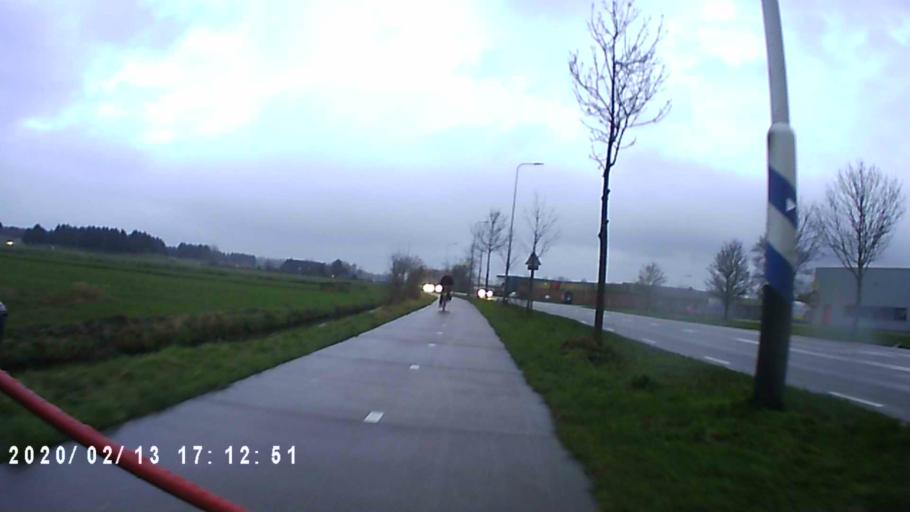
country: NL
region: Groningen
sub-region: Gemeente Groningen
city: Groningen
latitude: 53.2172
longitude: 6.5088
